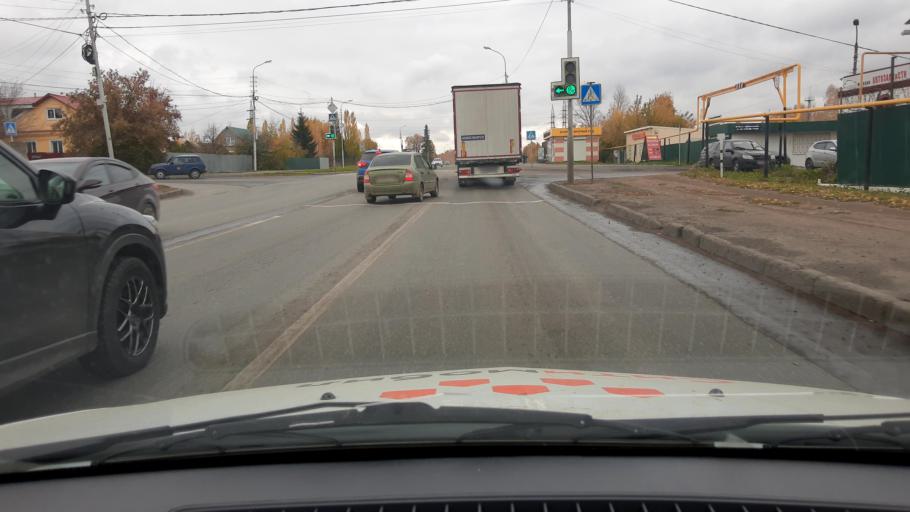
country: RU
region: Bashkortostan
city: Iglino
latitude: 54.7829
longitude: 56.2235
